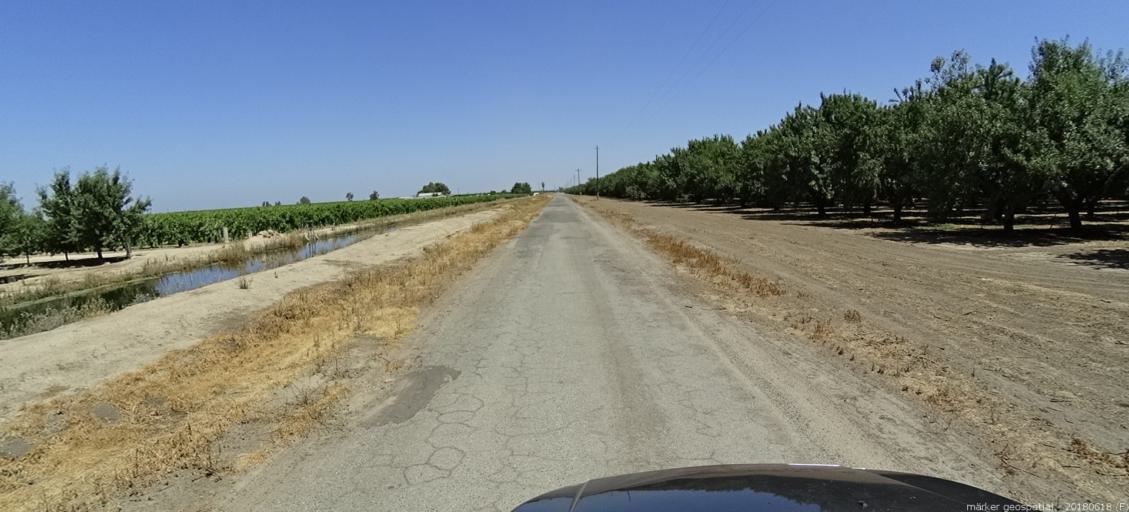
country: US
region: California
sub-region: Madera County
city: Parkwood
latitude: 36.8854
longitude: -120.1014
